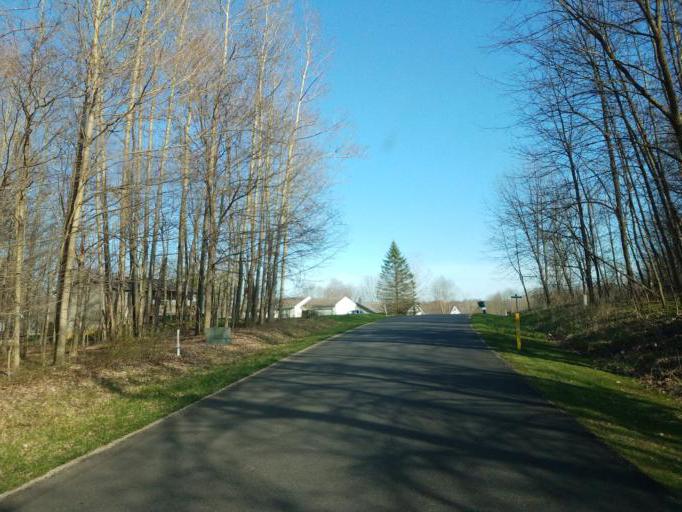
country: US
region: Ohio
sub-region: Knox County
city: Gambier
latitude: 40.4509
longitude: -82.3498
